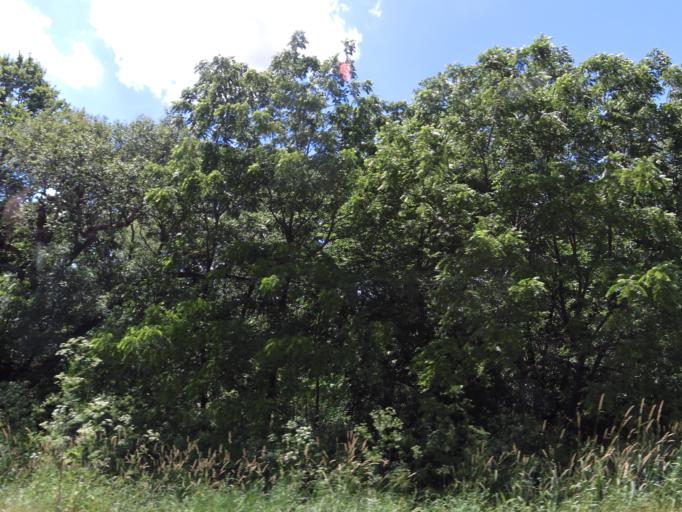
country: US
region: Iowa
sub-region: Buchanan County
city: Independence
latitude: 42.4990
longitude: -91.8896
